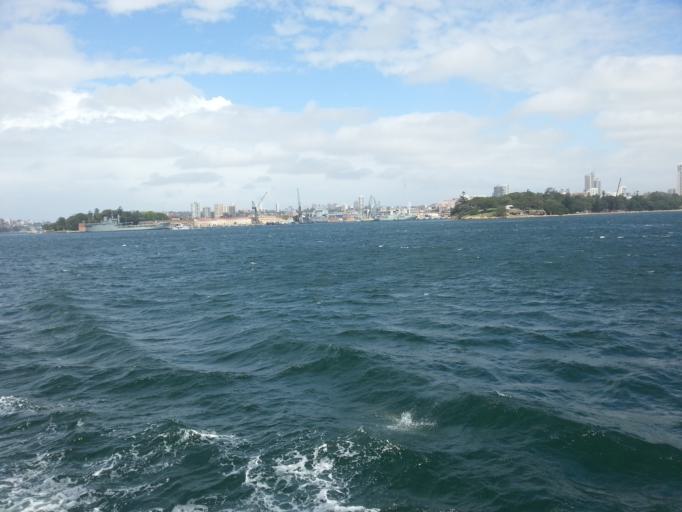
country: AU
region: New South Wales
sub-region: North Sydney
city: Kirribilli
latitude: -33.8532
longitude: 151.2202
